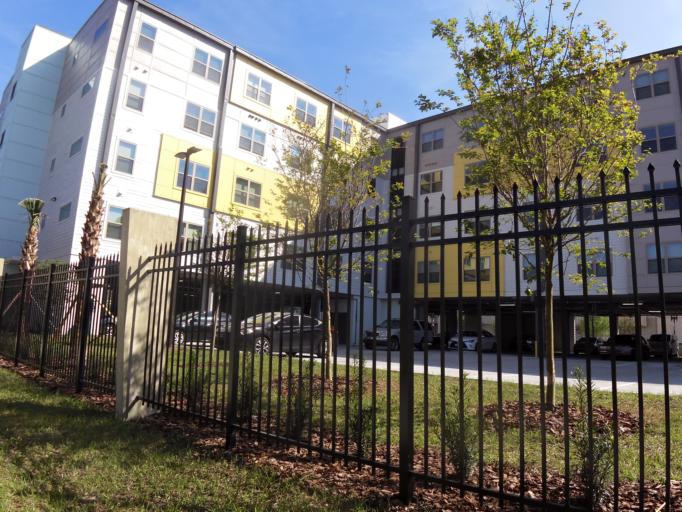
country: US
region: Florida
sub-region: Duval County
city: Jacksonville
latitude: 30.3280
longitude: -81.6695
